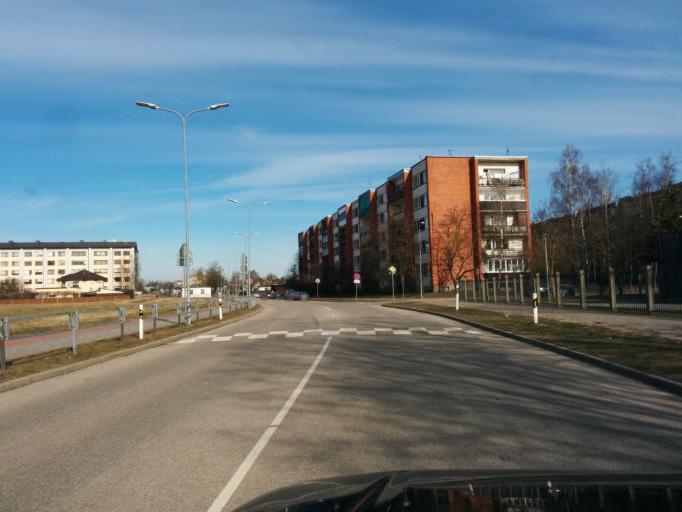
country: LV
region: Jelgava
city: Jelgava
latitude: 56.6406
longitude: 23.7200
